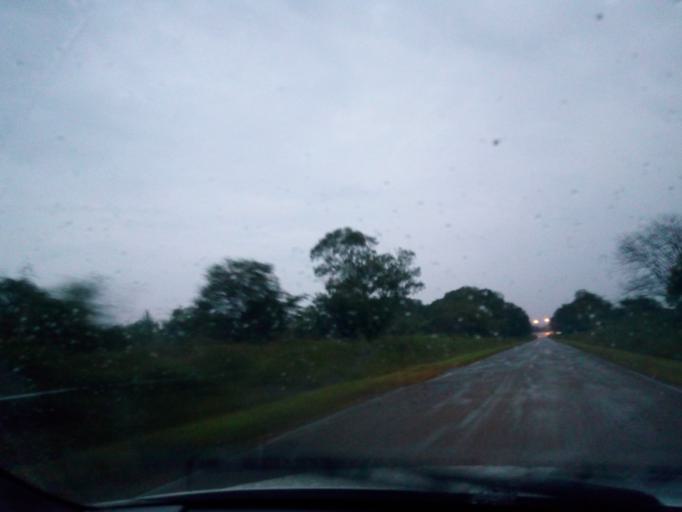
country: RU
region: Primorskiy
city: Lazo
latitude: 45.8701
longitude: 133.7148
